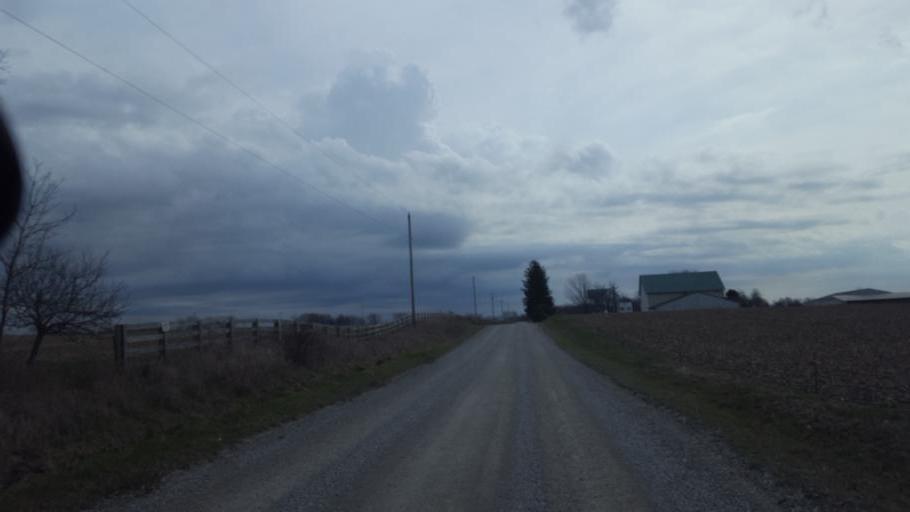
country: US
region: Ohio
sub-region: Morrow County
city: Mount Gilead
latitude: 40.5584
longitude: -82.7409
